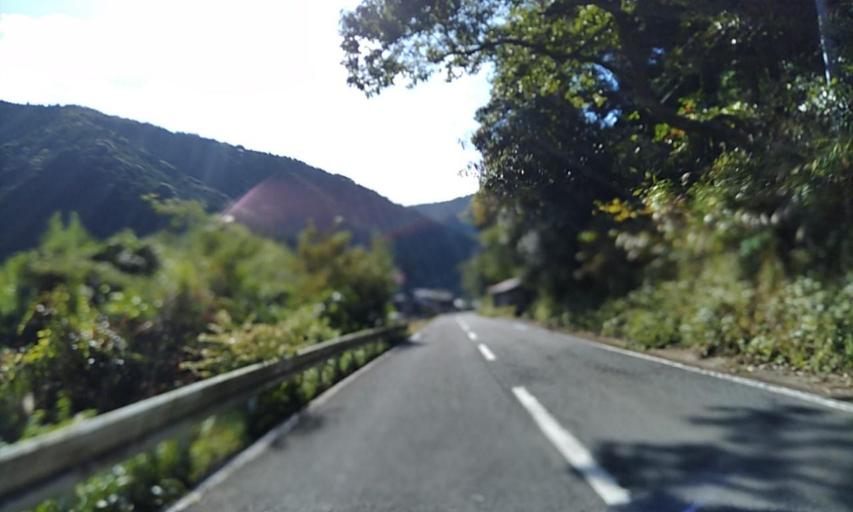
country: JP
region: Wakayama
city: Kainan
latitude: 34.0648
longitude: 135.3582
